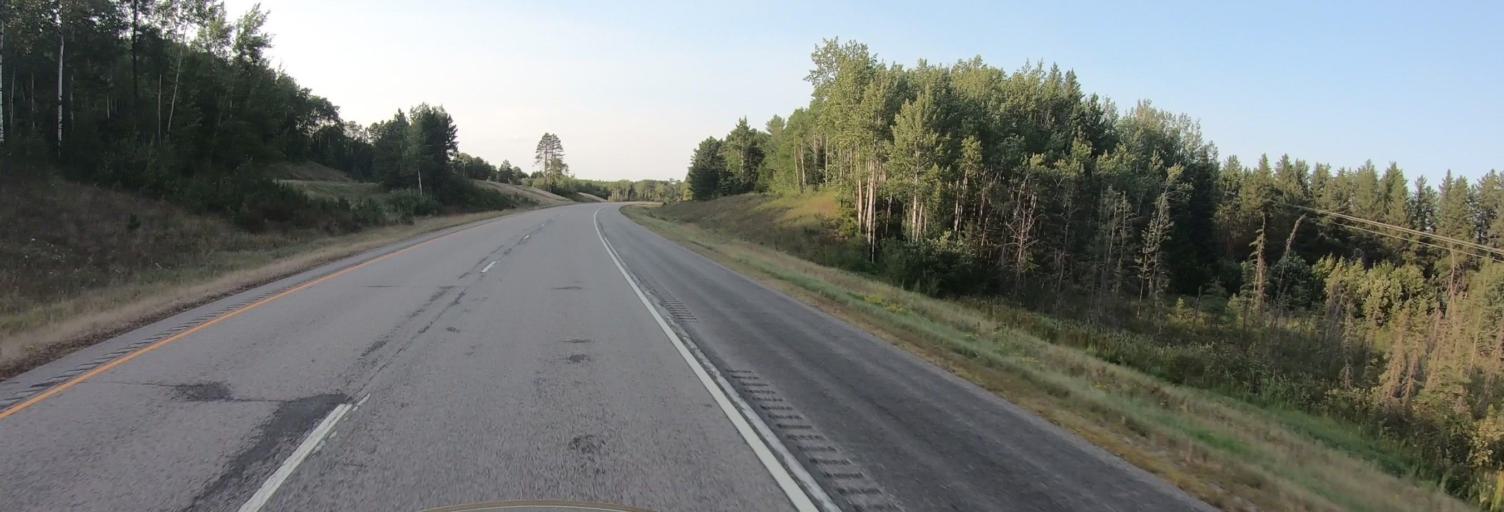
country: US
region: Minnesota
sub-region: Saint Louis County
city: Mountain Iron
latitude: 47.6831
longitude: -92.6386
